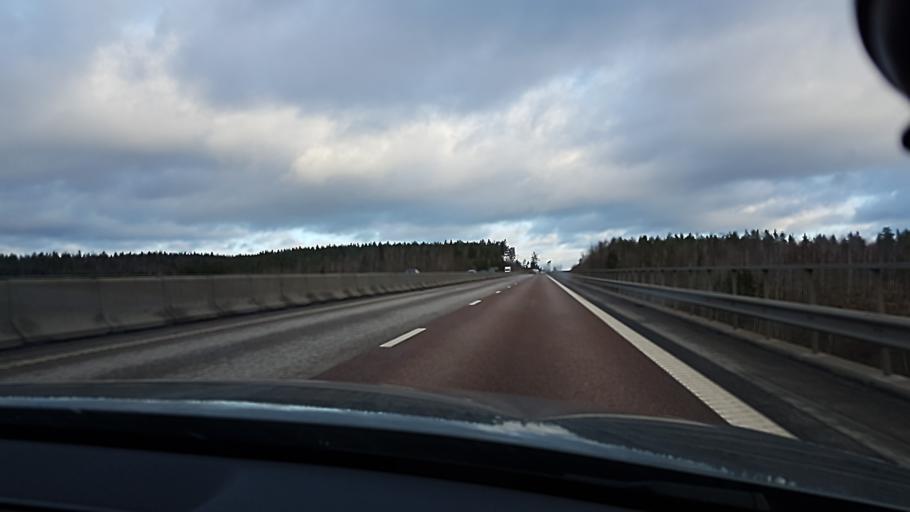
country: SE
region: OEstergoetland
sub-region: Norrkopings Kommun
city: Kimstad
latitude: 58.5099
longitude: 15.9921
